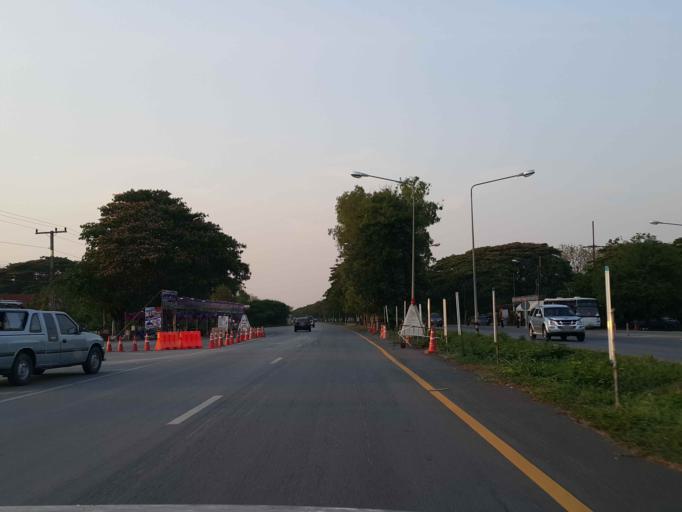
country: TH
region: Lampang
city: Sop Prap
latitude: 17.8982
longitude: 99.3408
